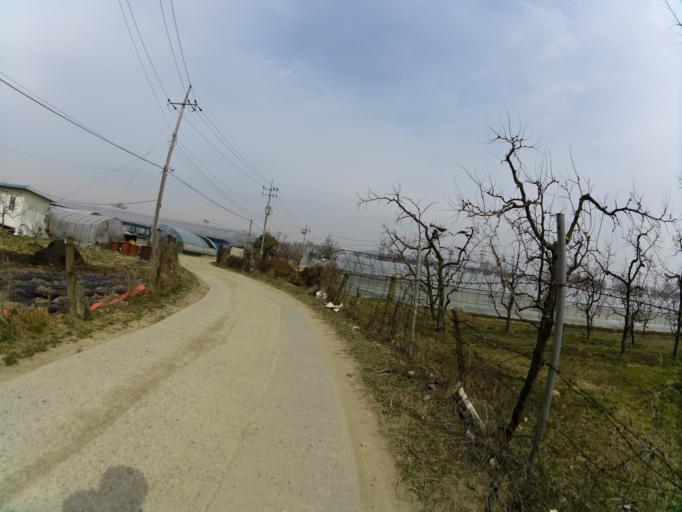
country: KR
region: Gyeongsangbuk-do
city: Gyeongsan-si
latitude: 35.8586
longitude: 128.7162
